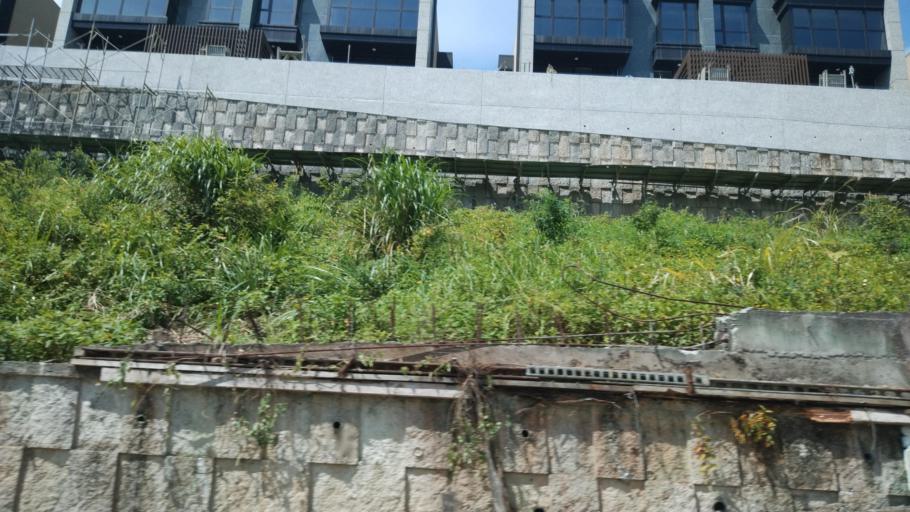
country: TW
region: Taipei
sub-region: Taipei
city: Banqiao
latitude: 24.9404
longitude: 121.5048
